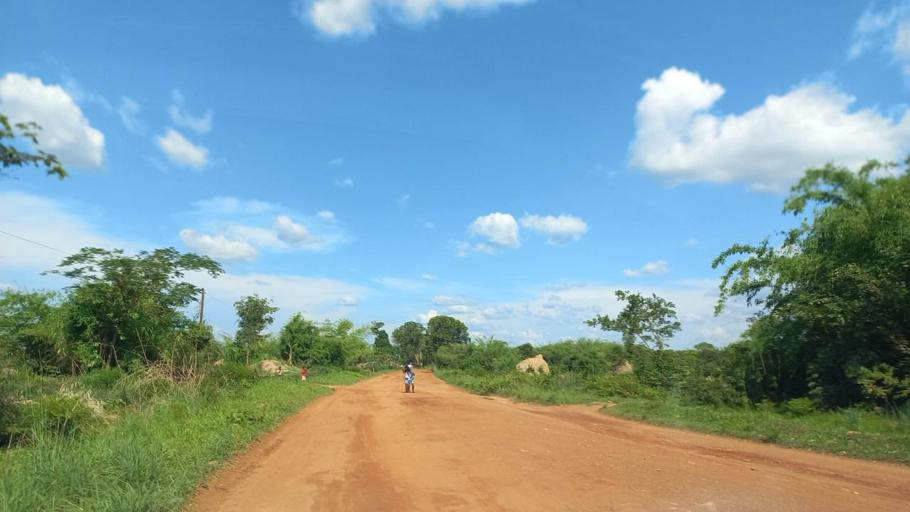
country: ZM
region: Copperbelt
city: Kitwe
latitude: -12.8649
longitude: 28.3734
